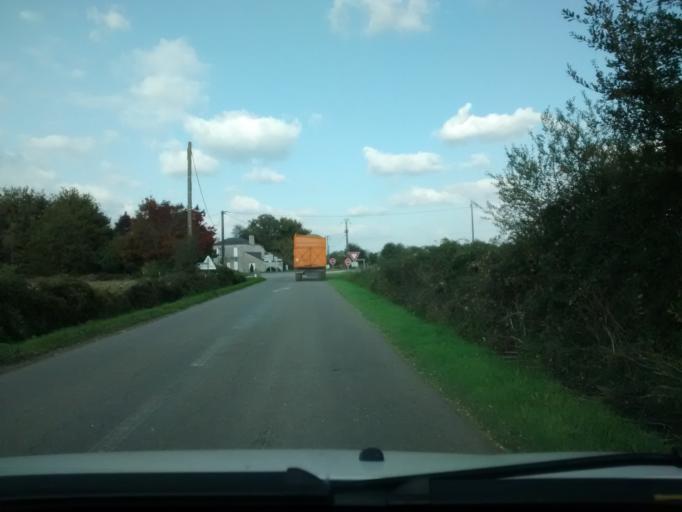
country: FR
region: Pays de la Loire
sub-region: Departement de la Loire-Atlantique
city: Sautron
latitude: 47.2888
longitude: -1.6577
